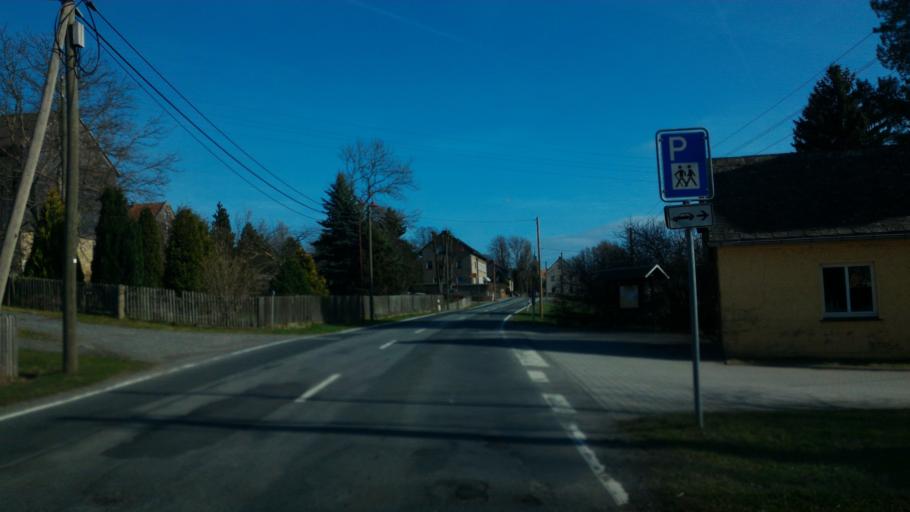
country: DE
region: Saxony
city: Stolpen
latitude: 51.0138
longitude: 14.0598
